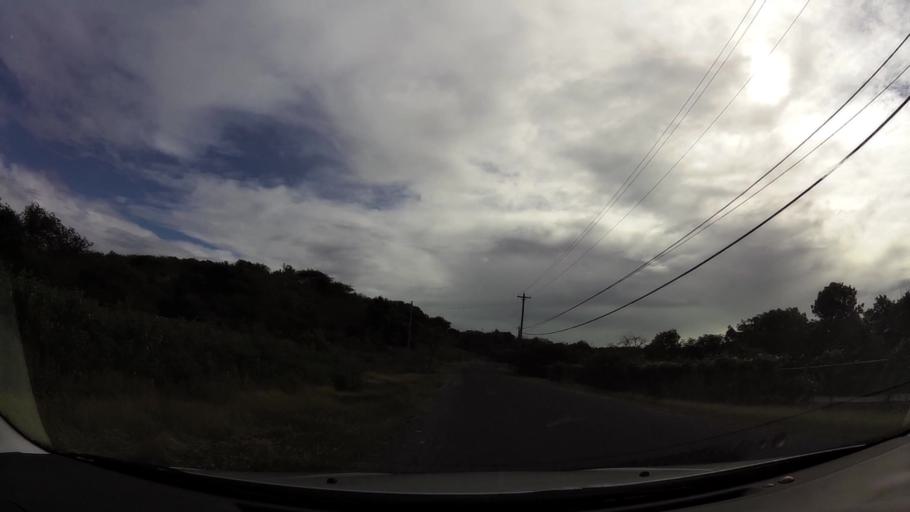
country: AG
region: Saint Peter
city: Parham
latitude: 17.0918
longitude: -61.6939
